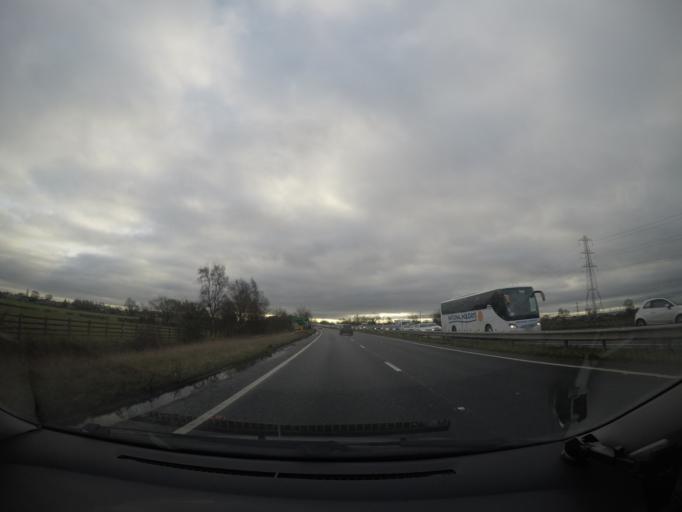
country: GB
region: England
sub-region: City of York
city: Murton
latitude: 53.9689
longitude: -1.0197
